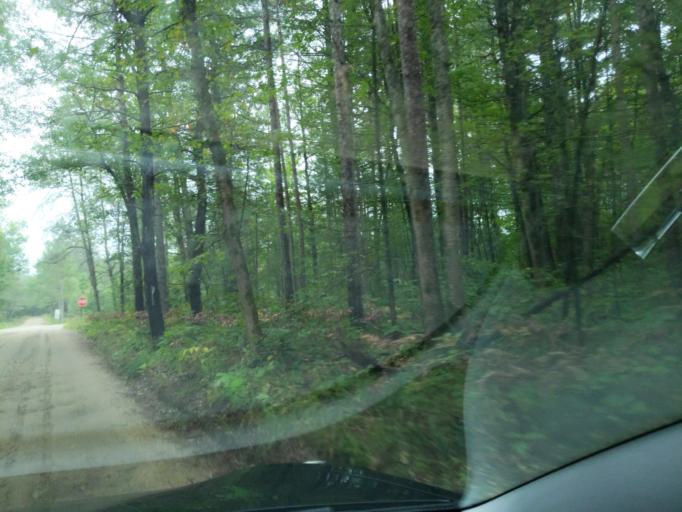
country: US
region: Michigan
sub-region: Grand Traverse County
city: Kingsley
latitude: 44.6942
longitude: -85.4077
